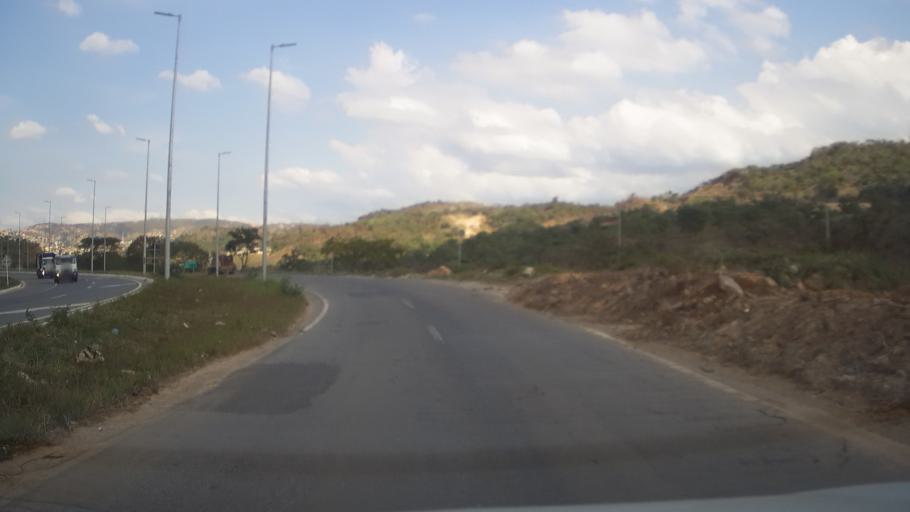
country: BR
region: Minas Gerais
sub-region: Belo Horizonte
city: Belo Horizonte
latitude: -19.8710
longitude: -43.8872
